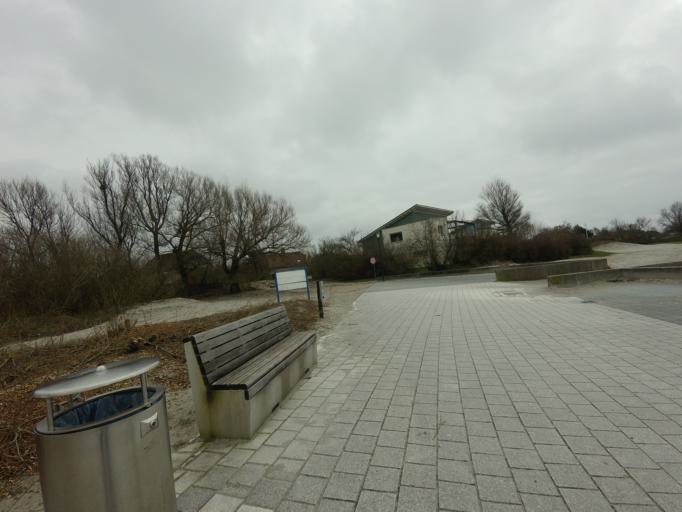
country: NL
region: Friesland
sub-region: Sudwest Fryslan
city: Makkum
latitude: 53.0479
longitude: 5.3812
